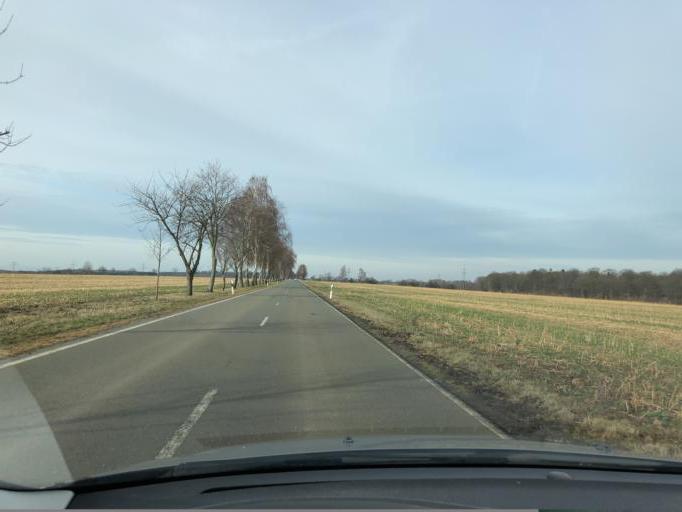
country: DE
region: Saxony-Anhalt
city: Bad Bibra
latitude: 51.1843
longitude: 11.5277
